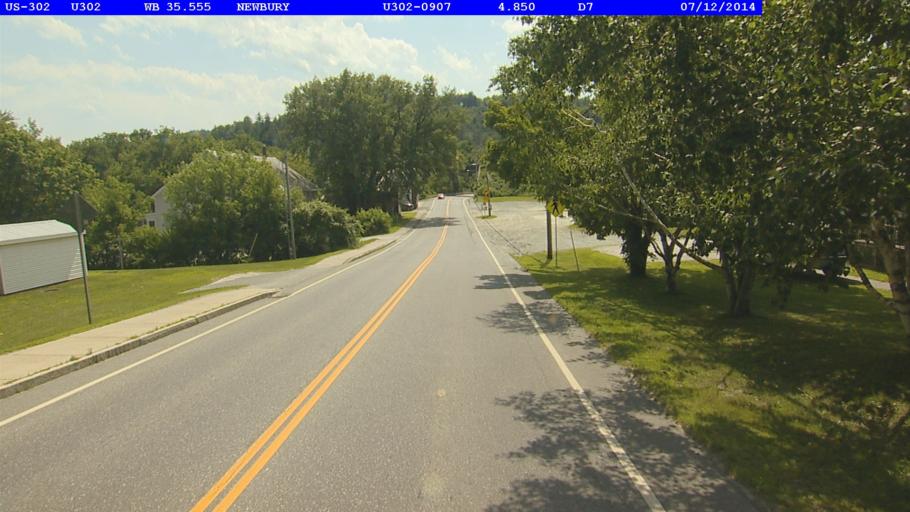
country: US
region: New Hampshire
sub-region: Grafton County
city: Woodsville
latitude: 44.1537
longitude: -72.0424
